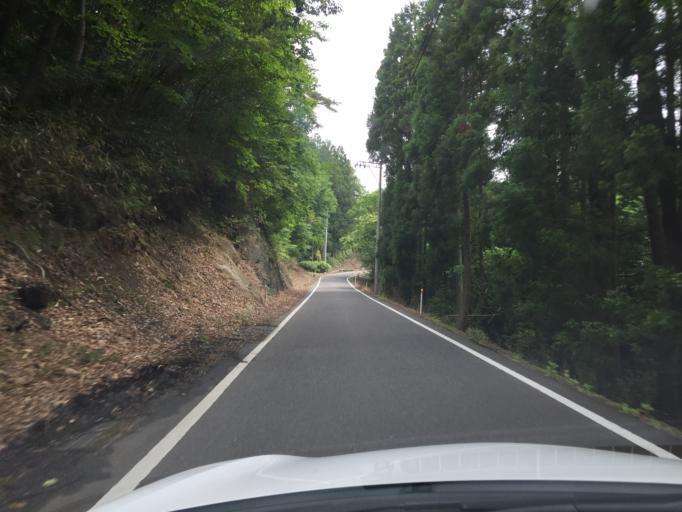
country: JP
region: Fukushima
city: Sukagawa
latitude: 37.2884
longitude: 140.5036
